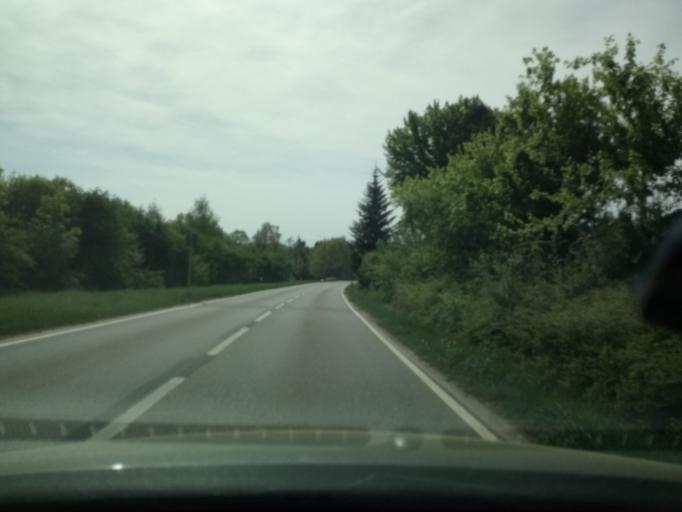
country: DE
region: Bavaria
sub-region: Upper Bavaria
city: Kraiburg am Inn
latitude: 48.1919
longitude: 12.4267
